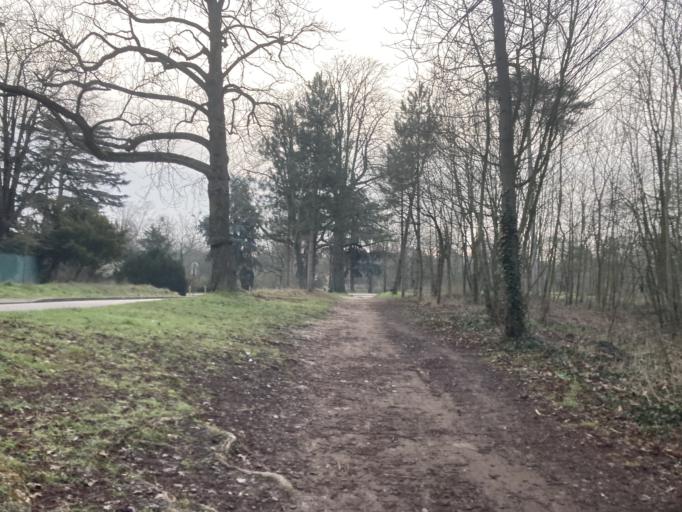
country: FR
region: Ile-de-France
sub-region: Departement des Hauts-de-Seine
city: Neuilly-sur-Seine
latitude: 48.8628
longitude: 2.2571
